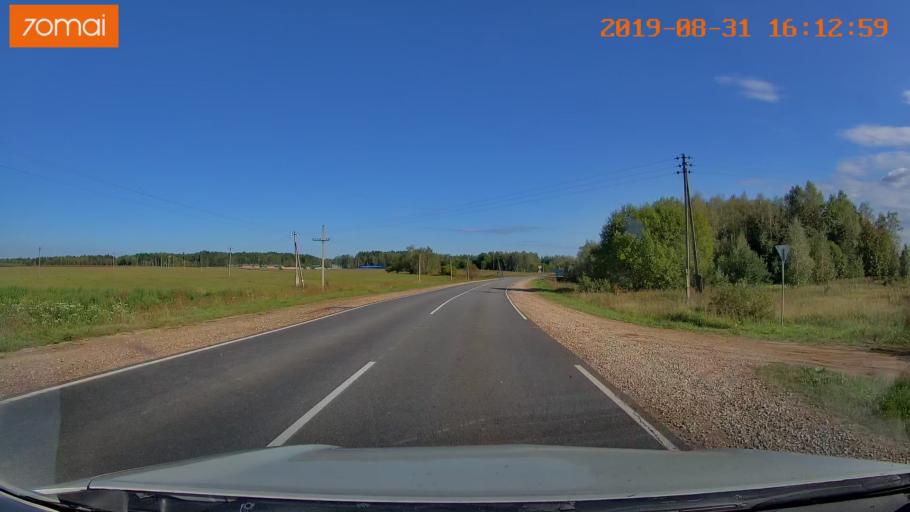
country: RU
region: Kaluga
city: Nikola-Lenivets
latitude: 54.5813
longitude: 35.4393
